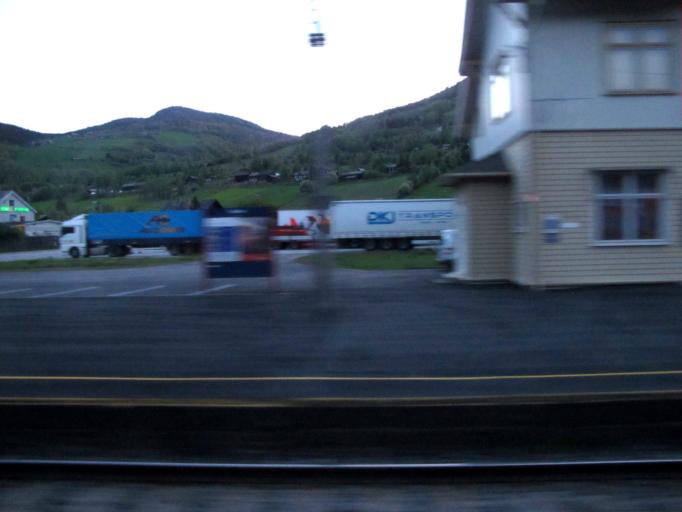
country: NO
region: Oppland
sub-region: Nord-Fron
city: Vinstra
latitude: 61.6647
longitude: 9.7016
